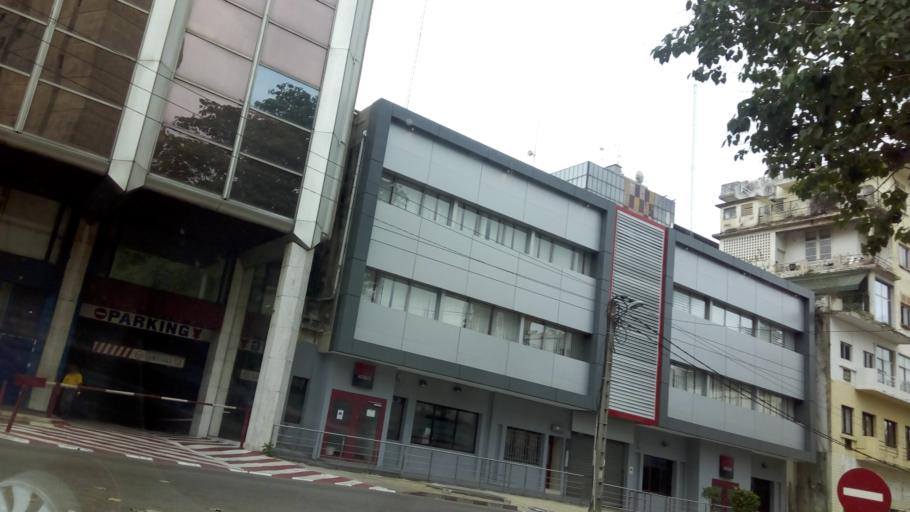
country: CI
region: Lagunes
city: Abidjan
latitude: 5.3219
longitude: -4.0161
